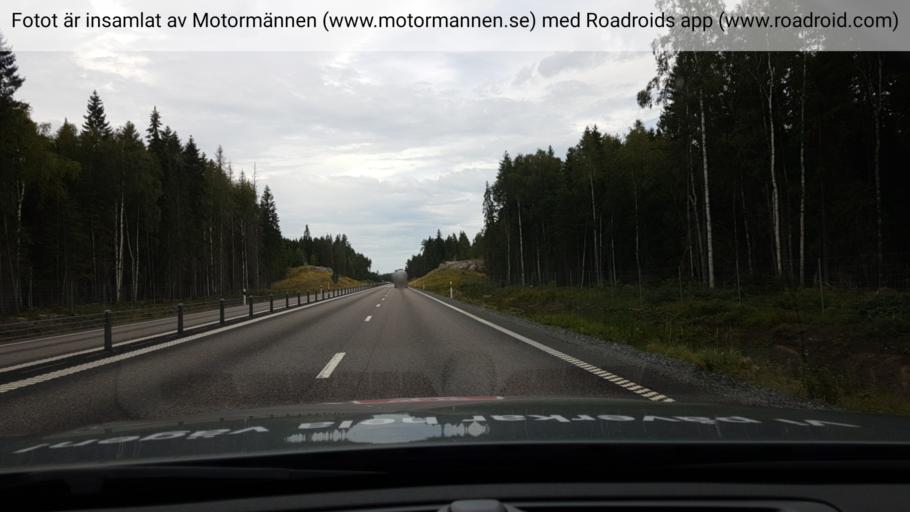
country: SE
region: Uppsala
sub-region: Heby Kommun
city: Tarnsjo
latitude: 60.0639
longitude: 16.9013
